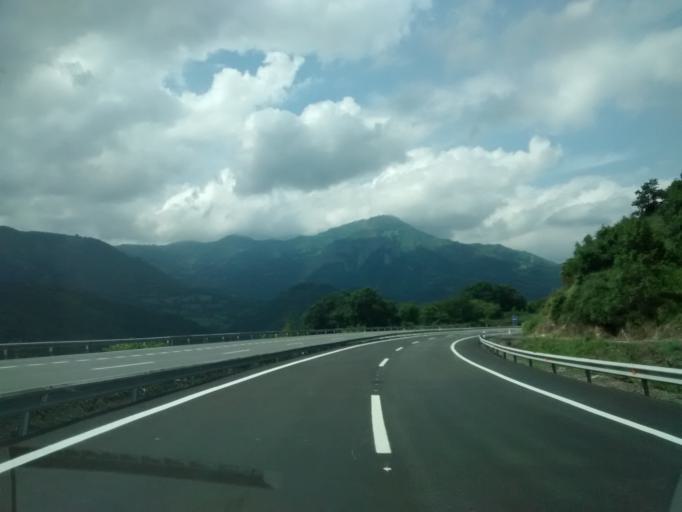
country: ES
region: Asturias
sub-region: Province of Asturias
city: Pola de Lena
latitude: 43.0669
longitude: -5.8250
